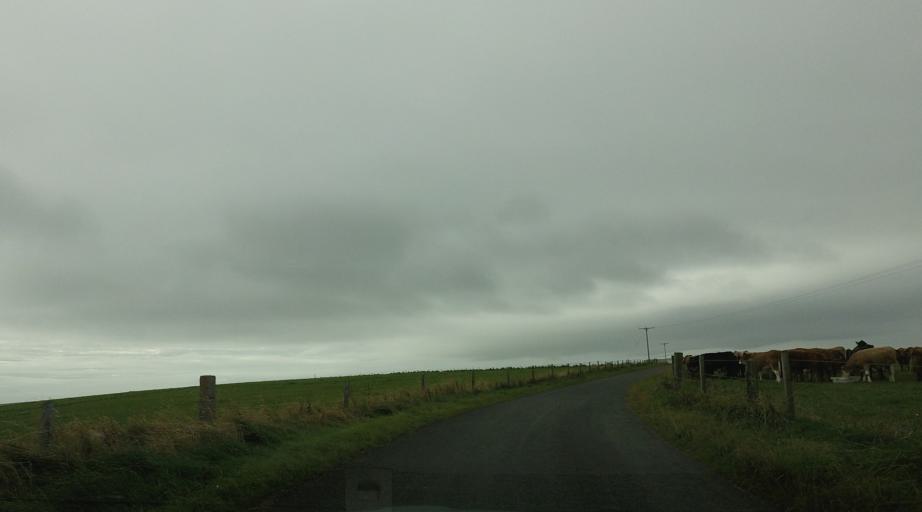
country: GB
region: Scotland
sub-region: Orkney Islands
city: Orkney
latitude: 58.8028
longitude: -2.9415
